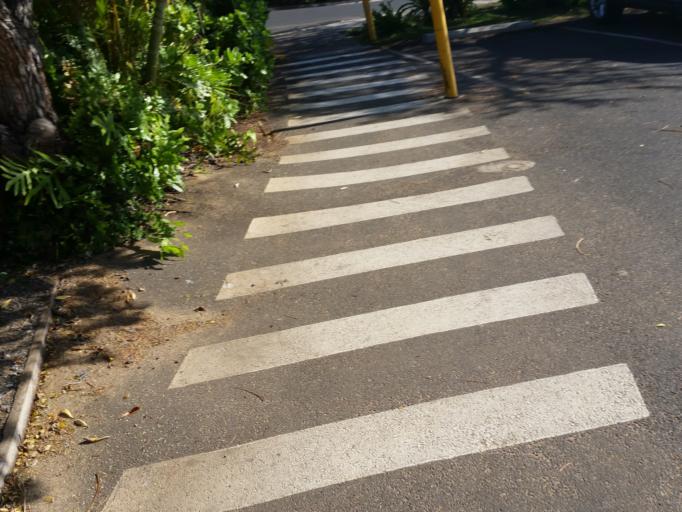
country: US
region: Hawaii
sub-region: Maui County
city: Ka'anapali
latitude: 20.9278
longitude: -156.6944
